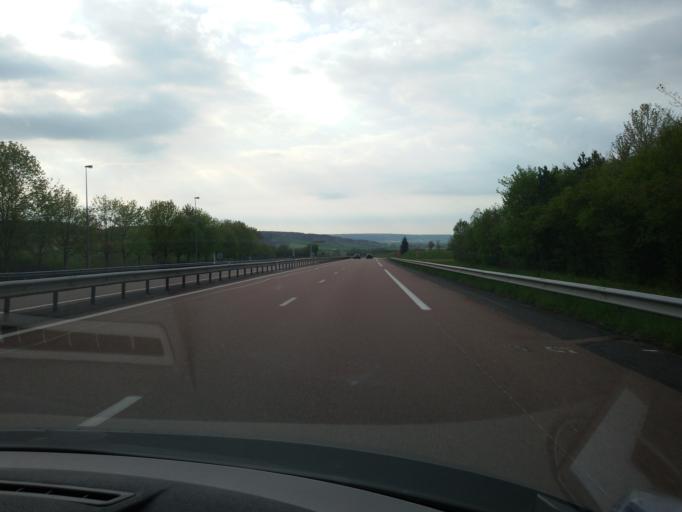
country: FR
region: Champagne-Ardenne
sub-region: Departement de la Haute-Marne
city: Chateauvillain
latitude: 48.0574
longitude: 4.9565
